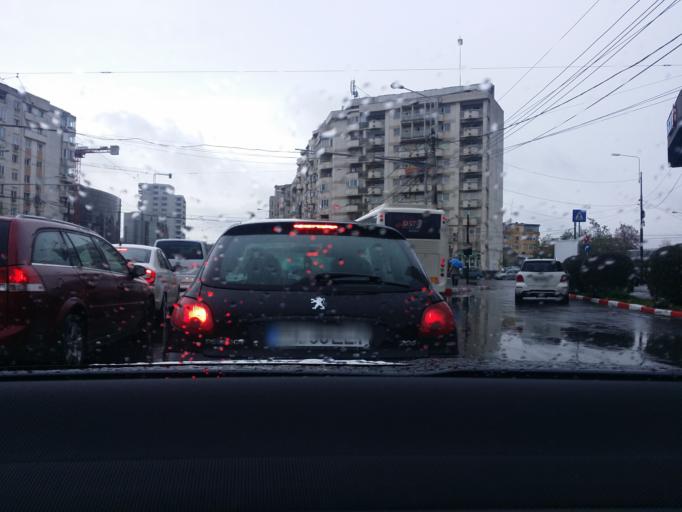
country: RO
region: Prahova
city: Ploiesti
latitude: 44.9458
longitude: 26.0194
